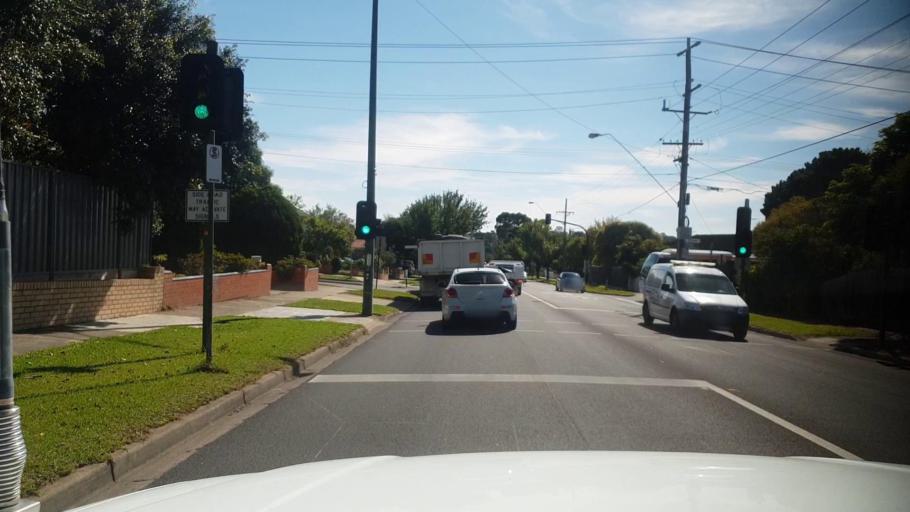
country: AU
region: Victoria
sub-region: Whitehorse
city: Blackburn North
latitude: -37.8036
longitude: 145.1415
